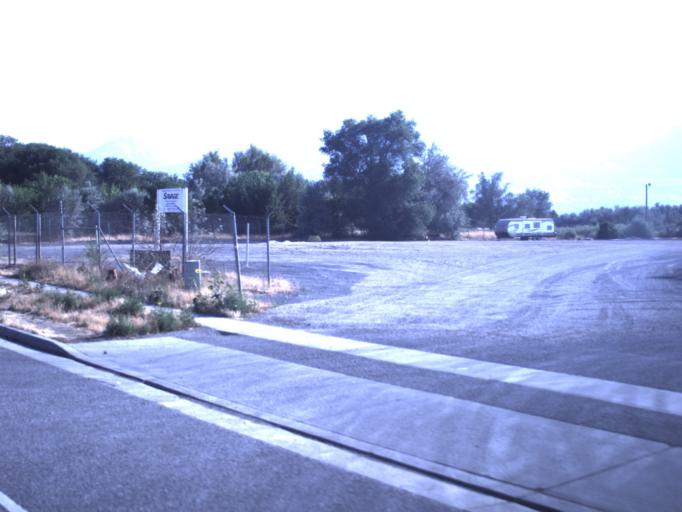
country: US
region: Utah
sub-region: Utah County
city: American Fork
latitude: 40.3650
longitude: -111.7854
